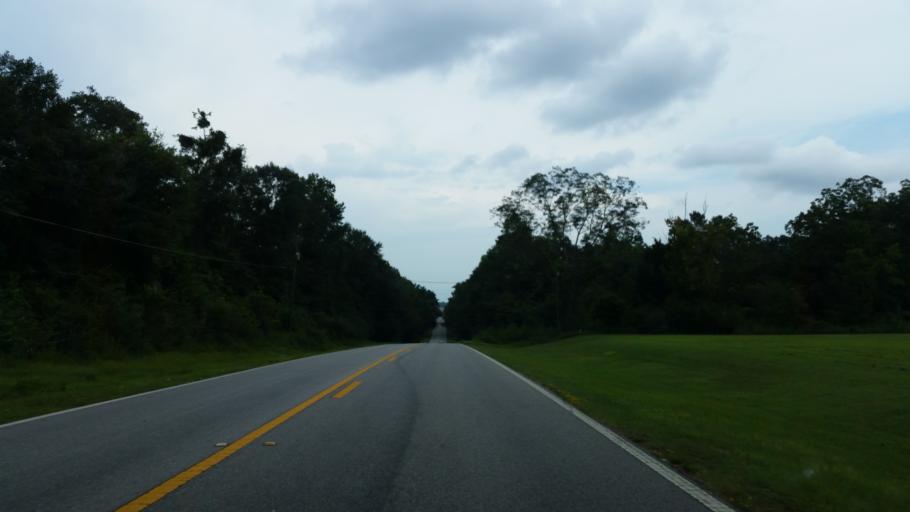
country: US
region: Florida
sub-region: Escambia County
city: Molino
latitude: 30.6808
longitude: -87.3666
